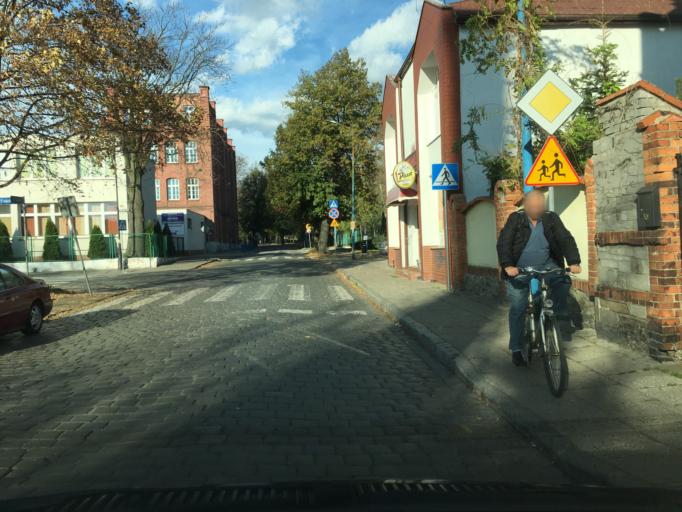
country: PL
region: Lower Silesian Voivodeship
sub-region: Powiat strzelinski
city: Strzelin
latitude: 50.7799
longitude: 17.0747
